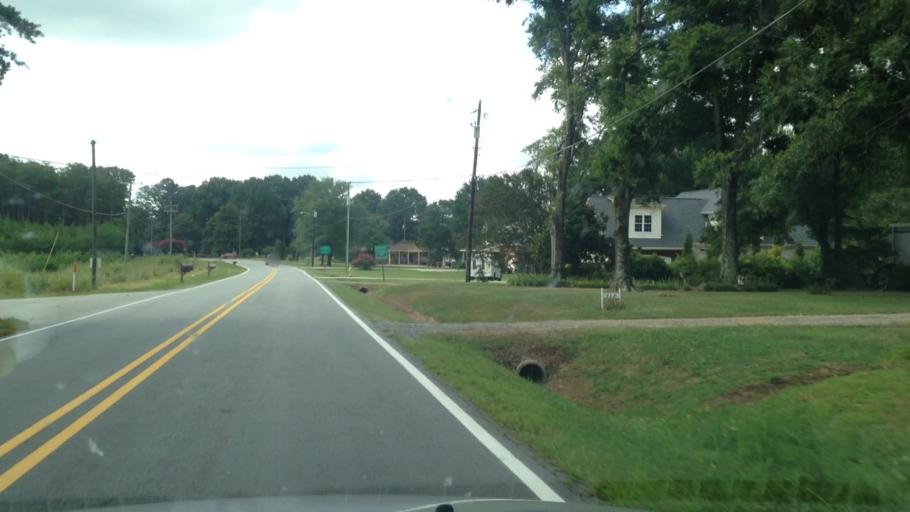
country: US
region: North Carolina
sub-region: Rockingham County
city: Madison
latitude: 36.3860
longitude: -80.0034
